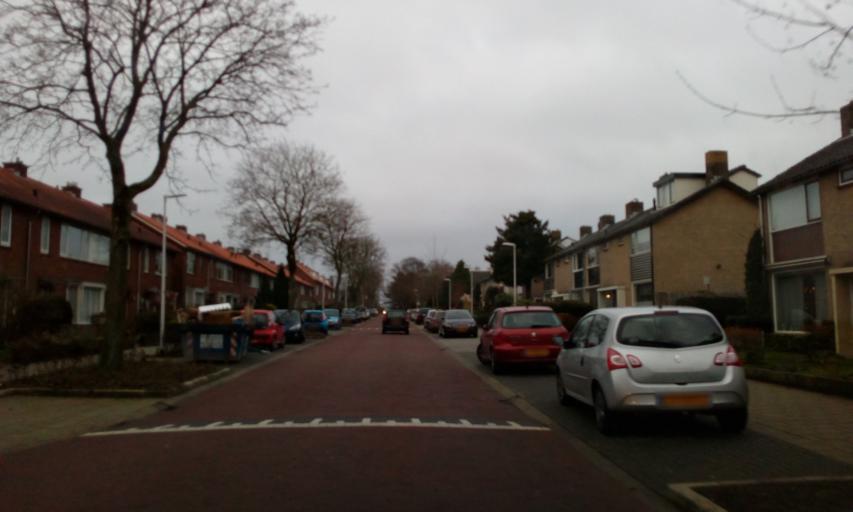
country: NL
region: North Holland
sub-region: Gemeente Bussum
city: Bussum
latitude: 52.2634
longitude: 5.1717
